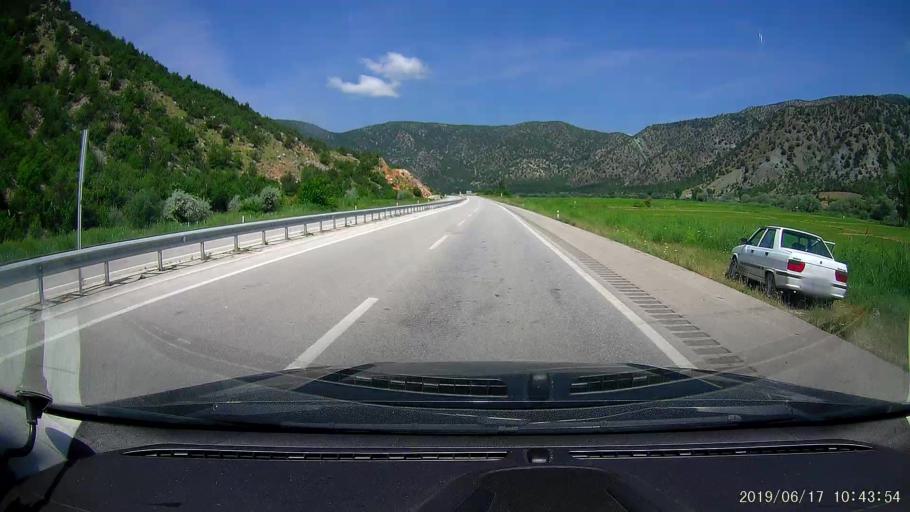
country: TR
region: Corum
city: Kargi
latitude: 41.0700
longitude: 34.5251
